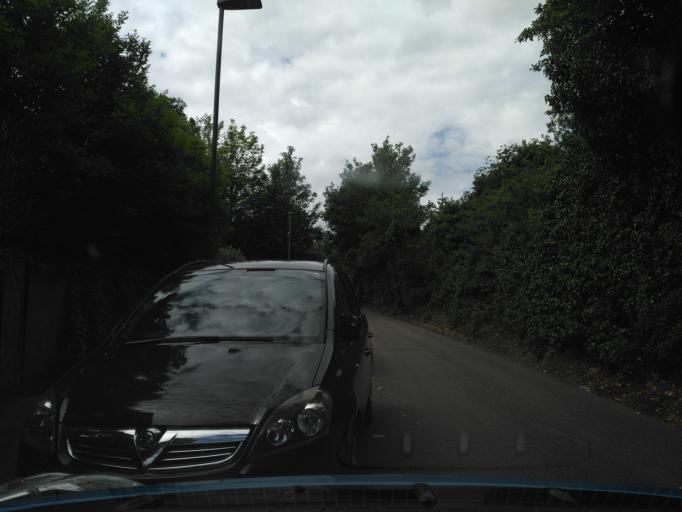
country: GB
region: England
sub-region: Greater London
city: Orpington
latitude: 51.3911
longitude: 0.1041
